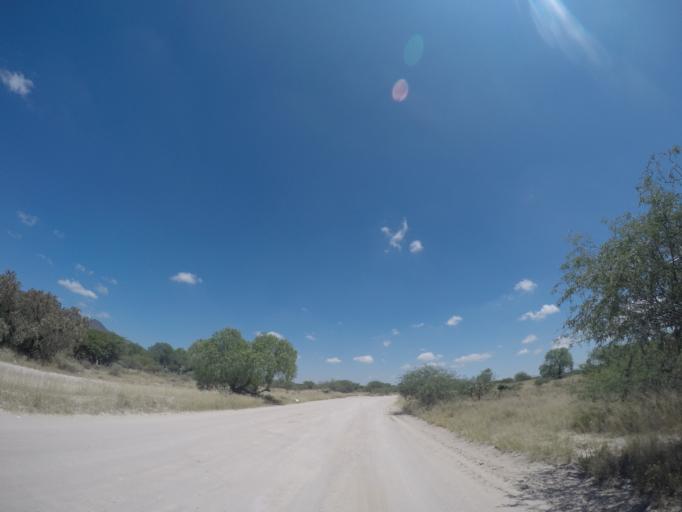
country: MX
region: San Luis Potosi
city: La Pila
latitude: 21.9892
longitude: -100.8994
